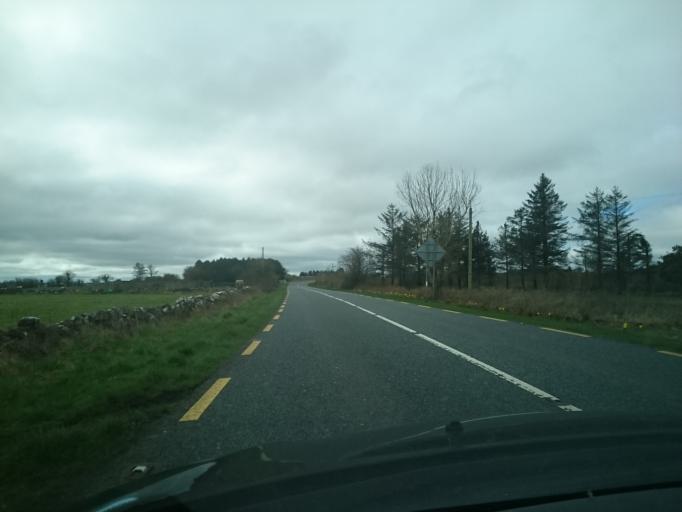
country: IE
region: Connaught
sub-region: Maigh Eo
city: Claremorris
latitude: 53.7189
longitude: -8.8862
